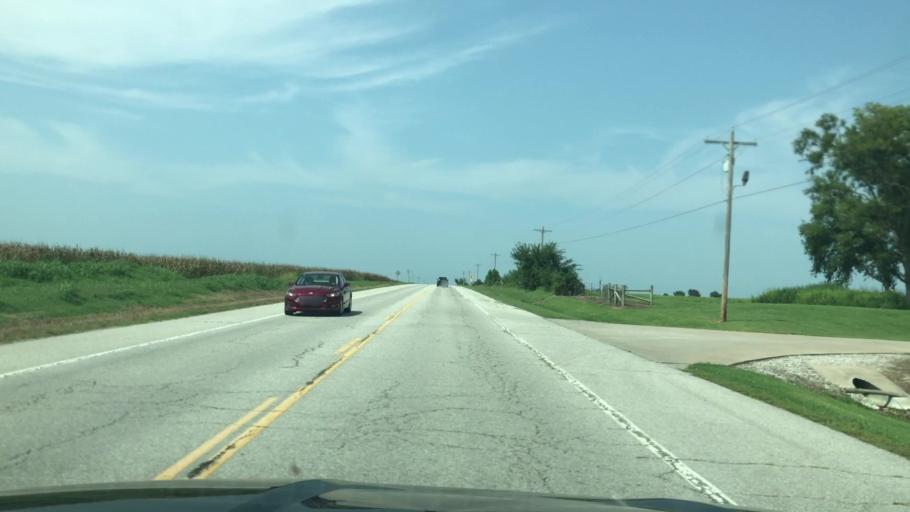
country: US
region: Oklahoma
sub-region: Ottawa County
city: Commerce
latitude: 36.9250
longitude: -94.8419
